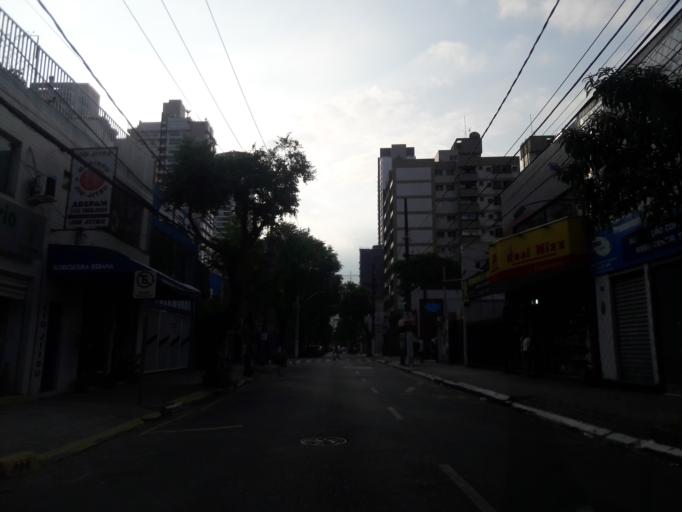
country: BR
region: Sao Paulo
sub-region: Santos
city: Santos
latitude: -23.9652
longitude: -46.3404
